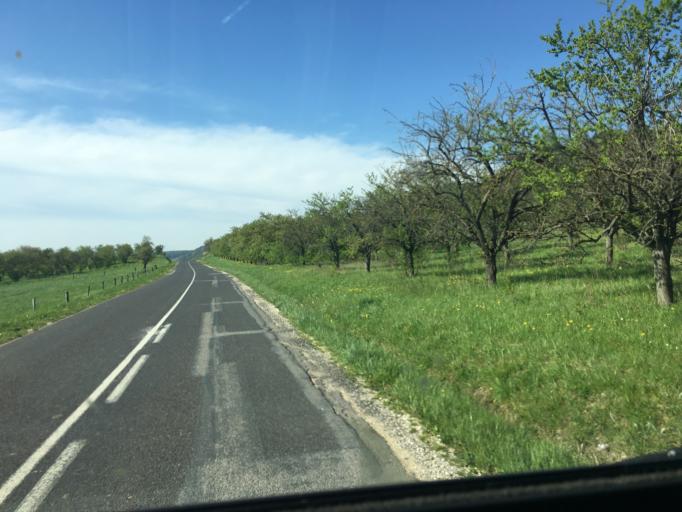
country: FR
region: Lorraine
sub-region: Departement de la Meuse
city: Vigneulles-les-Hattonchatel
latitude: 48.9218
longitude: 5.6828
